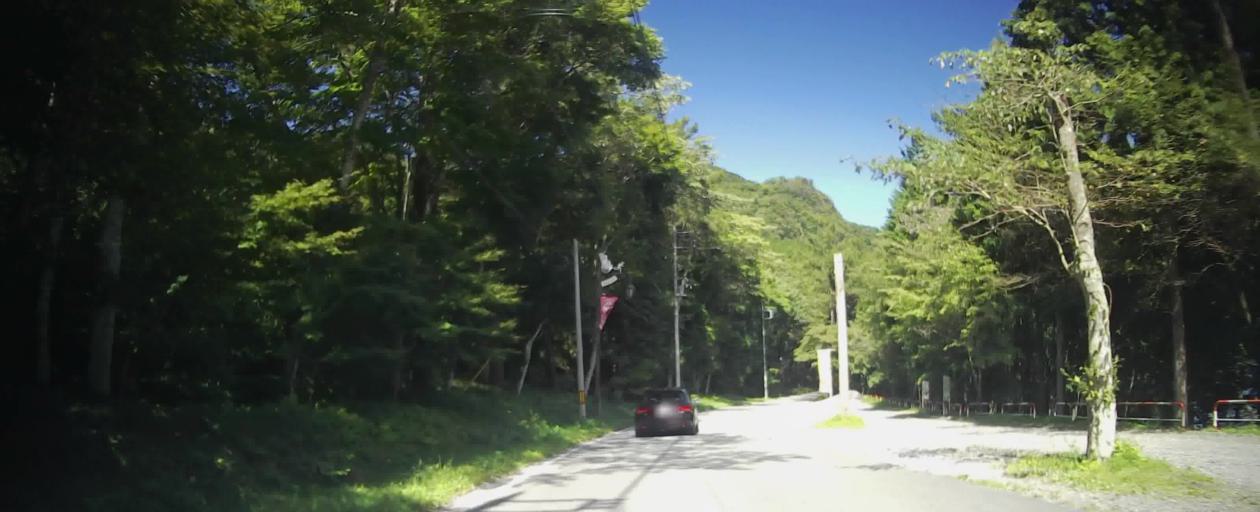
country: JP
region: Gunma
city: Nakanojomachi
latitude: 36.4778
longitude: 138.8611
